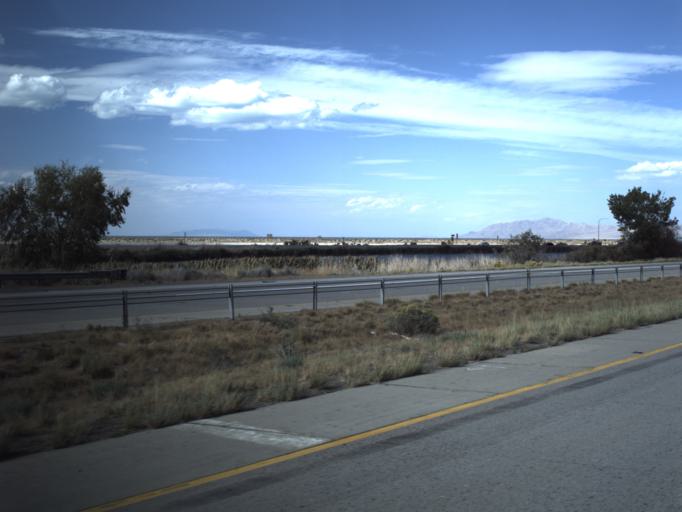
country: US
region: Utah
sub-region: Tooele County
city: Stansbury park
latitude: 40.6940
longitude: -112.2631
